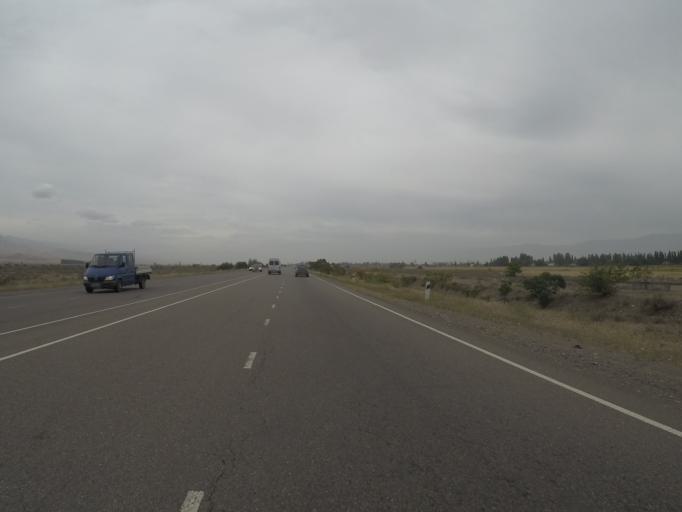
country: KG
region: Chuy
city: Bystrovka
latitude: 42.8287
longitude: 75.5330
